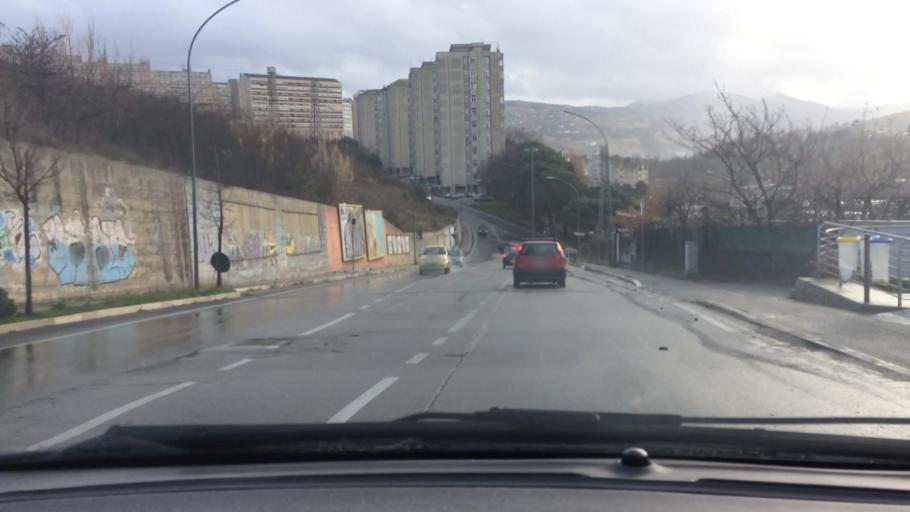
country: IT
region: Basilicate
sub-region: Provincia di Potenza
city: Potenza
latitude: 40.6368
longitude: 15.7869
